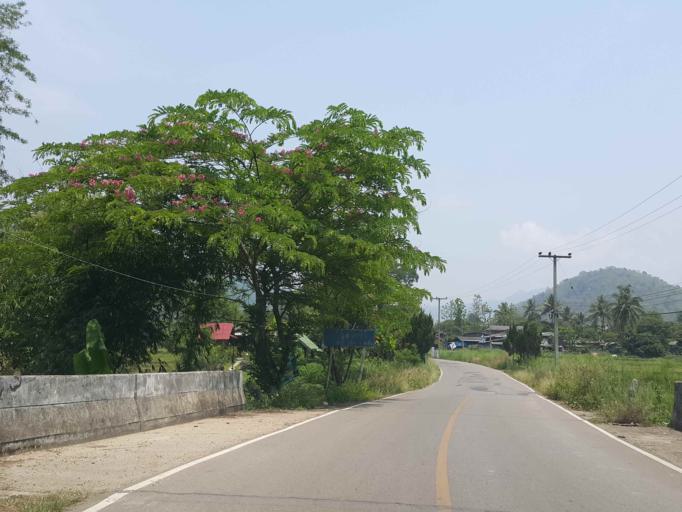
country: TH
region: Chiang Mai
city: Mae Taeng
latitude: 19.1665
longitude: 98.8593
